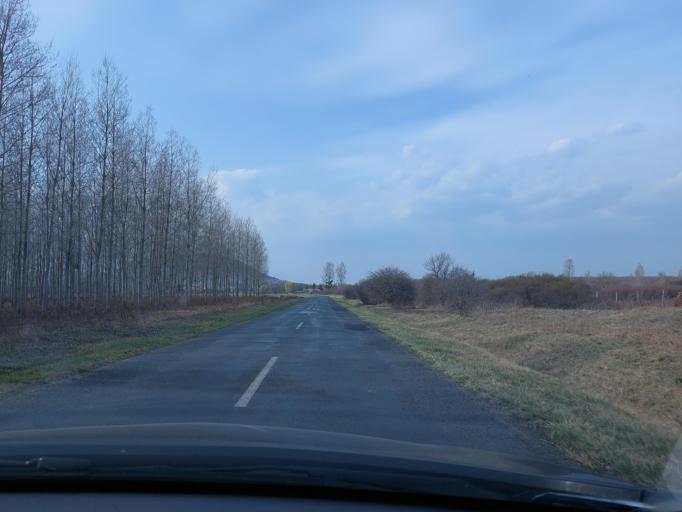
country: HU
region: Veszprem
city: Devecser
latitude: 47.1250
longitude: 17.4076
